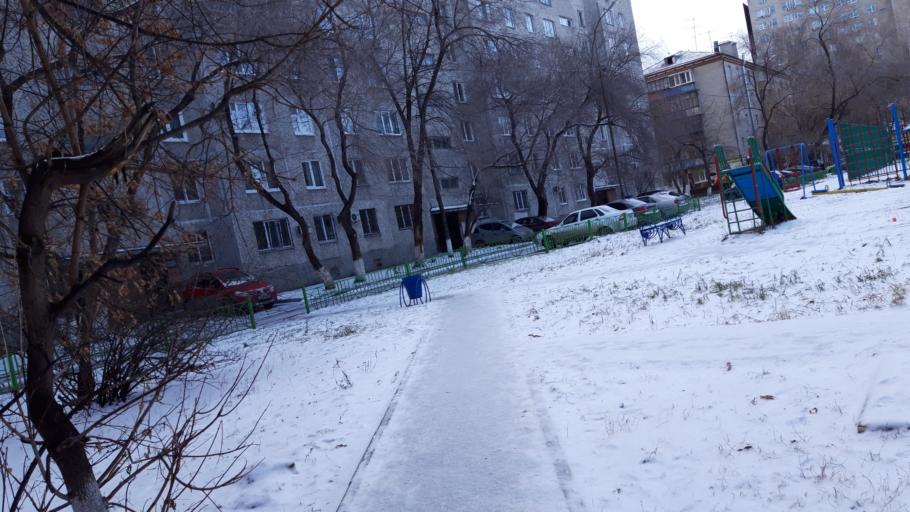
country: RU
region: Tjumen
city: Tyumen
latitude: 57.1507
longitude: 65.5513
